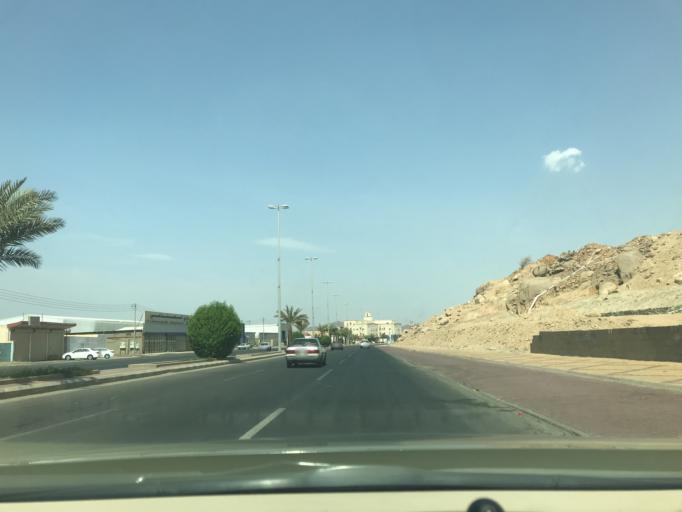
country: SA
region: Makkah
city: Al Jumum
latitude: 21.6246
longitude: 39.6756
